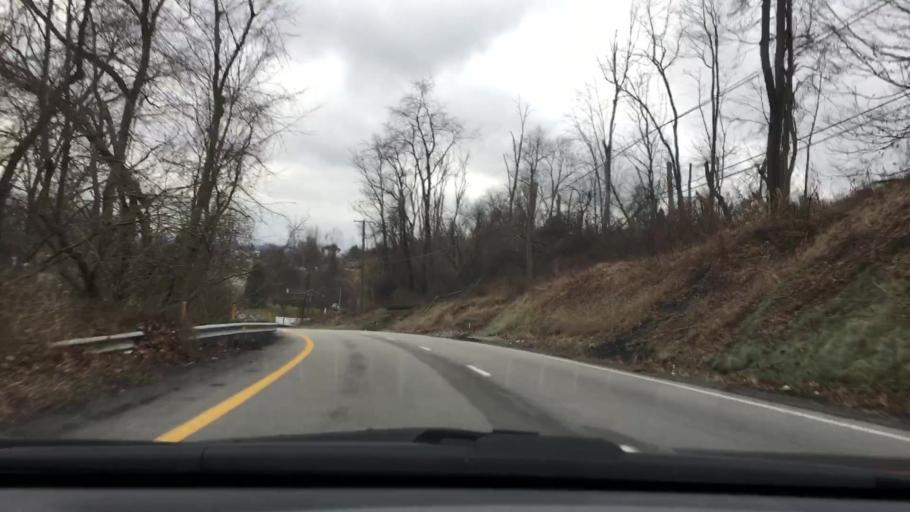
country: US
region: Pennsylvania
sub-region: Fayette County
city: Oliver
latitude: 39.9438
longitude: -79.7337
